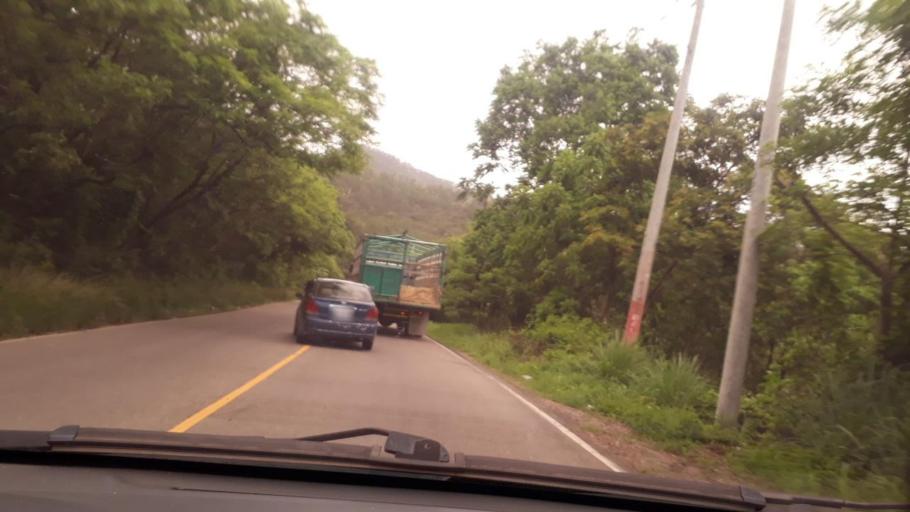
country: GT
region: Chiquimula
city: Concepcion Las Minas
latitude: 14.5628
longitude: -89.4533
